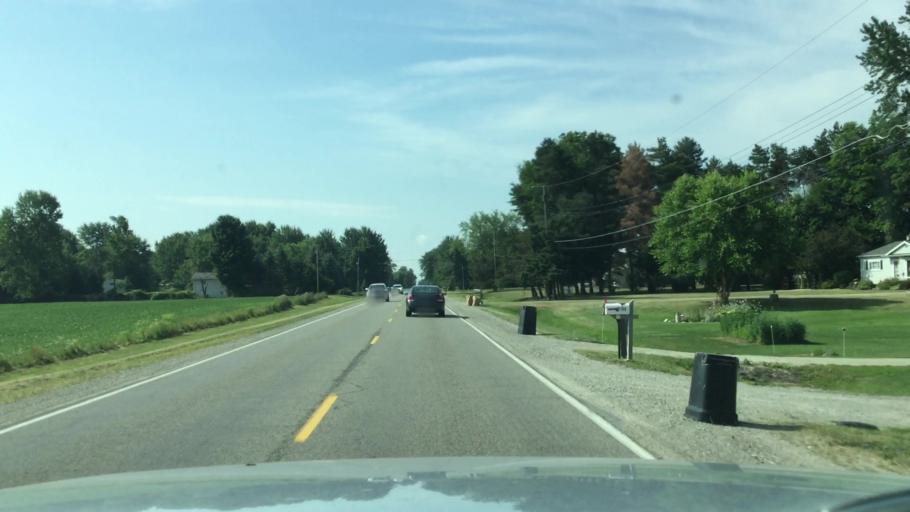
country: US
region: Michigan
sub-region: Genesee County
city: Flushing
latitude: 43.1091
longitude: -83.8137
